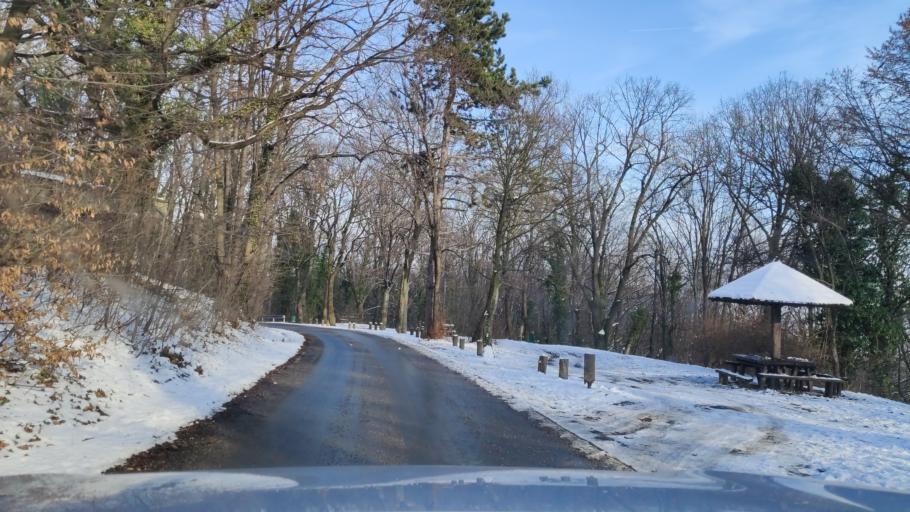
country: RS
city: Rusanj
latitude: 44.6961
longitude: 20.5153
